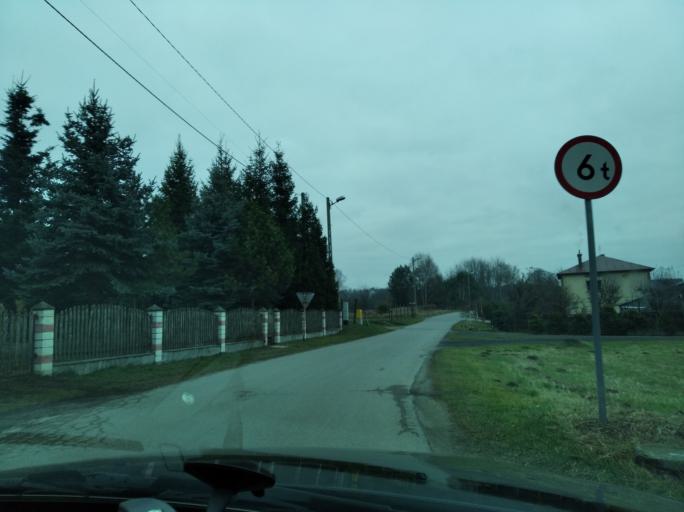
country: PL
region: Subcarpathian Voivodeship
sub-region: Powiat lancucki
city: Rakszawa
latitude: 50.1525
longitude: 22.2349
